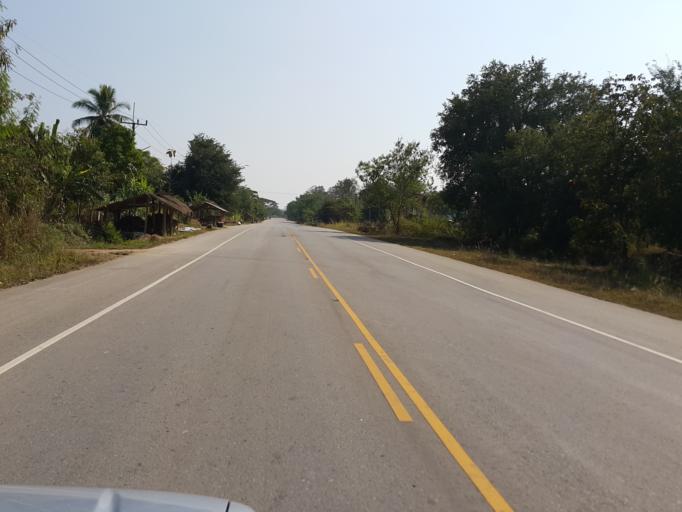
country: TH
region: Lampang
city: Mueang Pan
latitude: 18.8579
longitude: 99.5979
